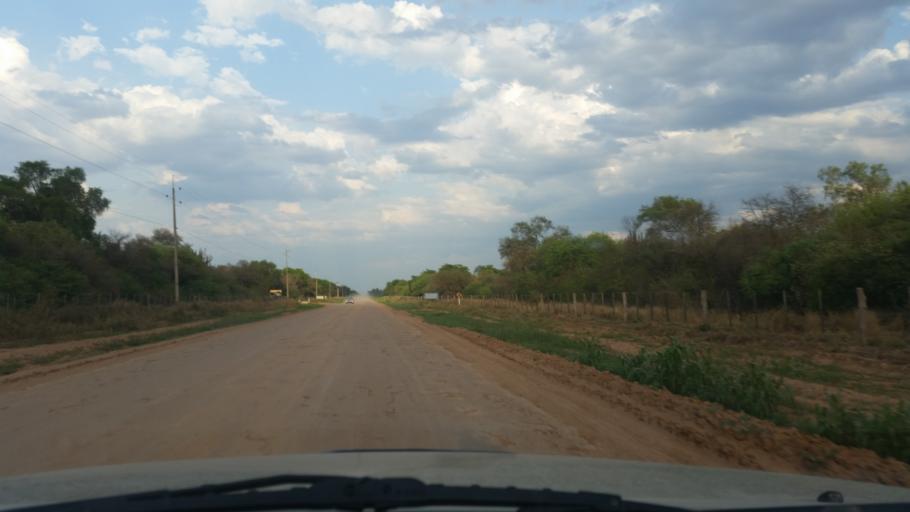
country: PY
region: Boqueron
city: Filadelfia
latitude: -22.3488
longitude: -59.9429
